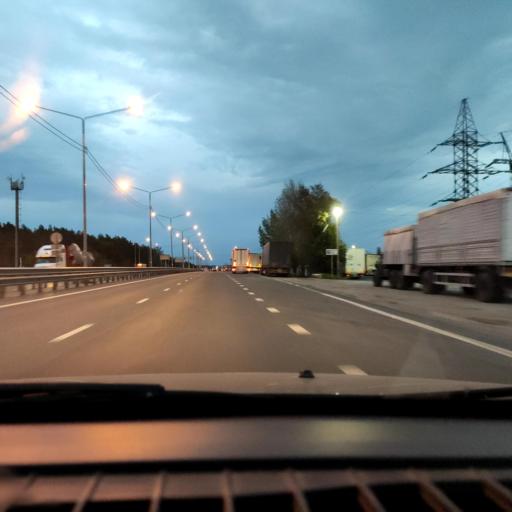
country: RU
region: Samara
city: Zhigulevsk
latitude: 53.5137
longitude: 49.6098
